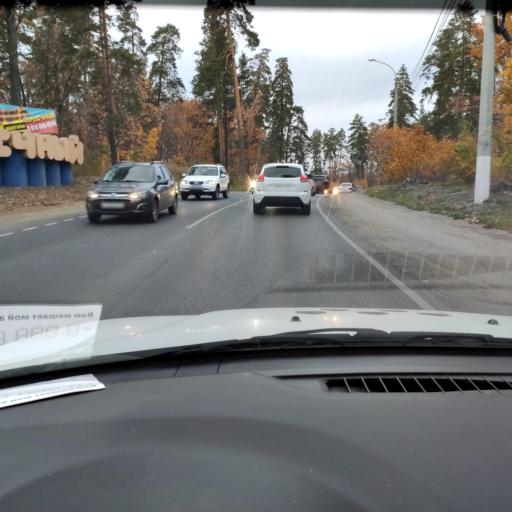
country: RU
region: Samara
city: Tol'yatti
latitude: 53.4894
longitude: 49.3071
